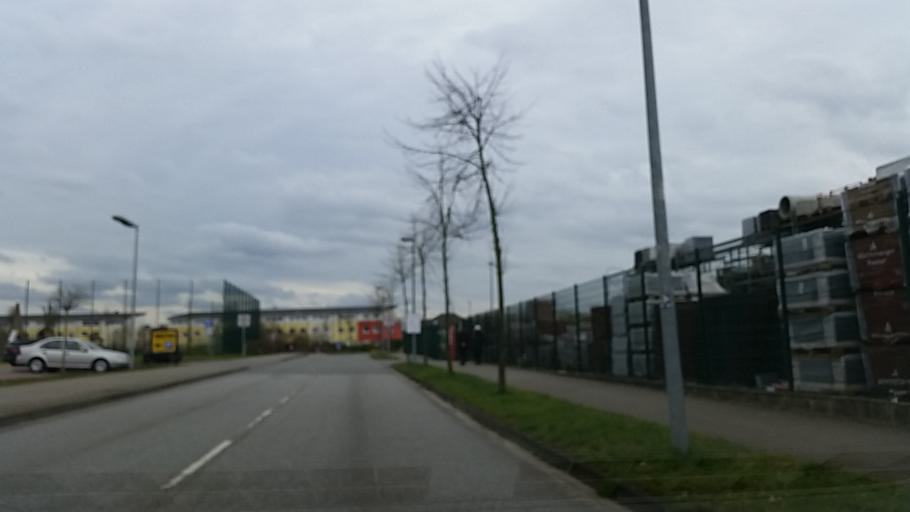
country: DE
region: Schleswig-Holstein
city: Glinde
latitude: 53.5449
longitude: 10.2269
